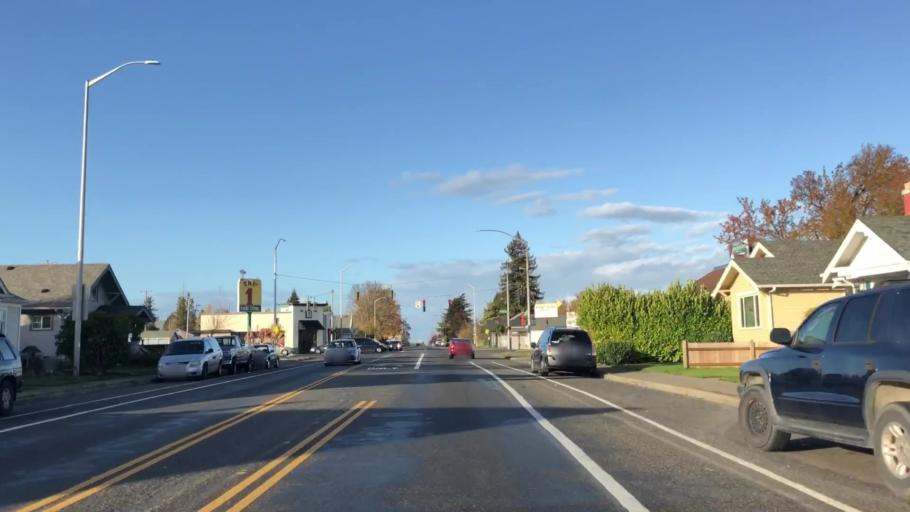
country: US
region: Washington
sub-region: Pierce County
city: Tacoma
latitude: 47.2055
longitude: -122.4432
